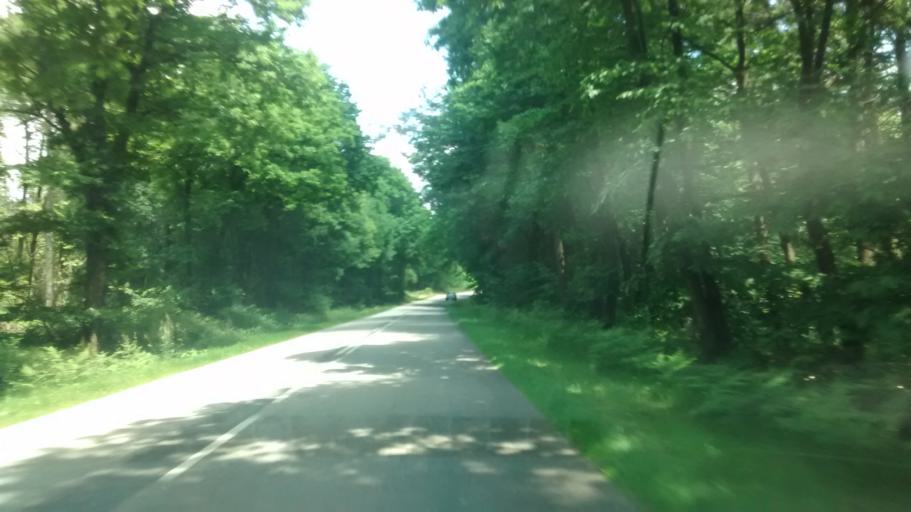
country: FR
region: Brittany
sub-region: Departement du Morbihan
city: Guer
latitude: 47.8875
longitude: -2.1742
